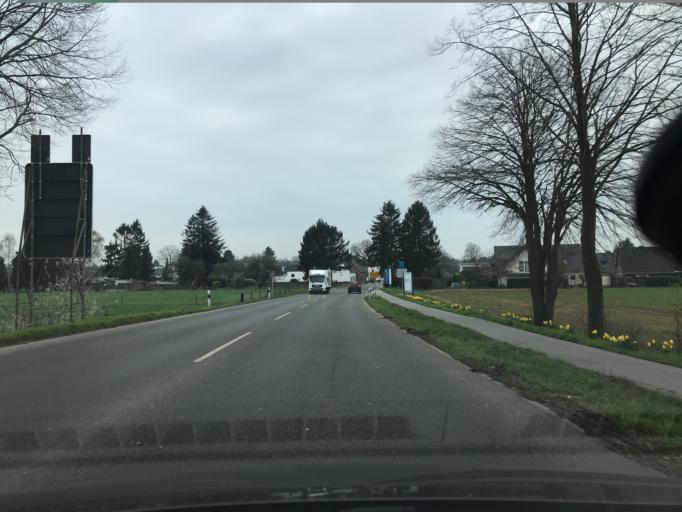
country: DE
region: North Rhine-Westphalia
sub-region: Regierungsbezirk Dusseldorf
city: Viersen
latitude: 51.2702
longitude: 6.3480
